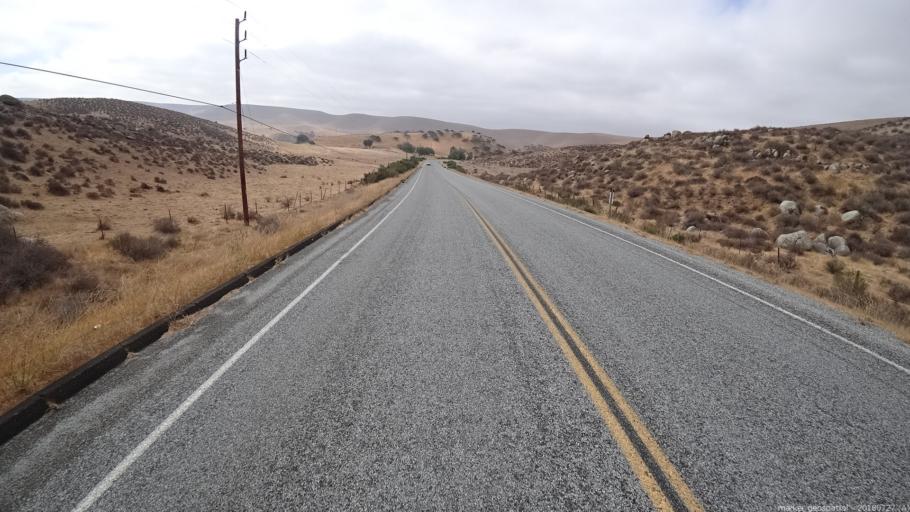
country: US
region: California
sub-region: Monterey County
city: King City
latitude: 36.2752
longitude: -121.0646
